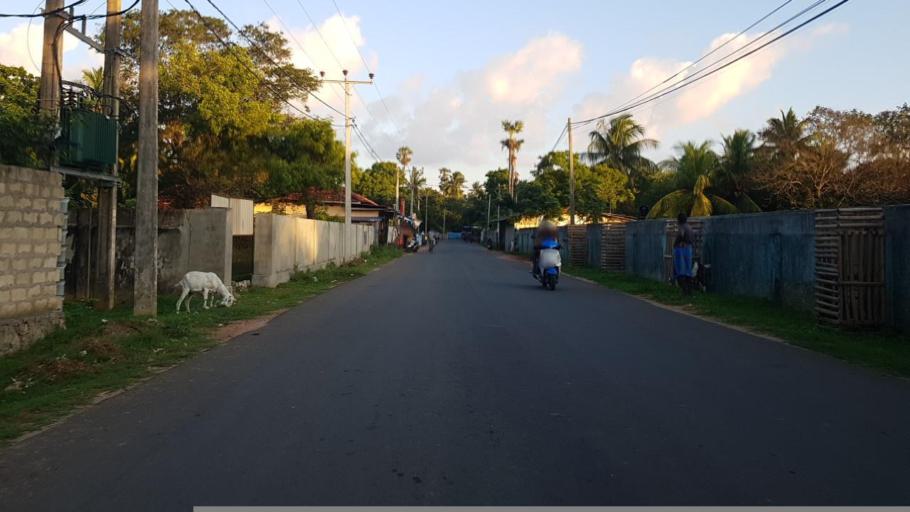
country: LK
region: Northern Province
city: Jaffna
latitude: 9.7170
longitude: 79.9829
